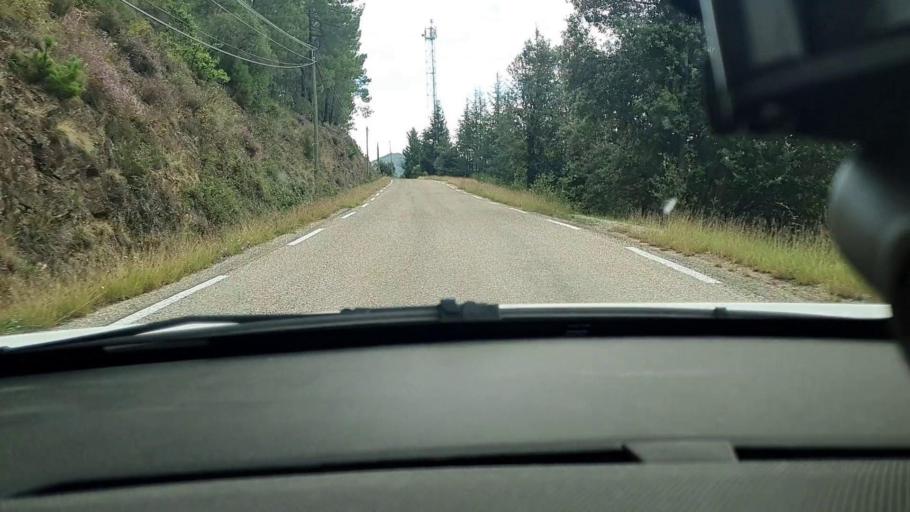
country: FR
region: Languedoc-Roussillon
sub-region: Departement du Gard
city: Branoux-les-Taillades
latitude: 44.3129
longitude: 3.9965
